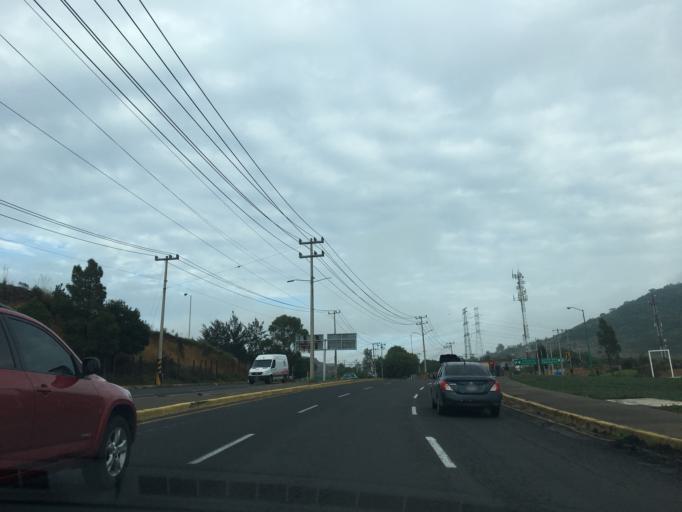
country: MX
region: Mexico
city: Ciudad Lopez Mateos
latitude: 19.5455
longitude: -99.2754
